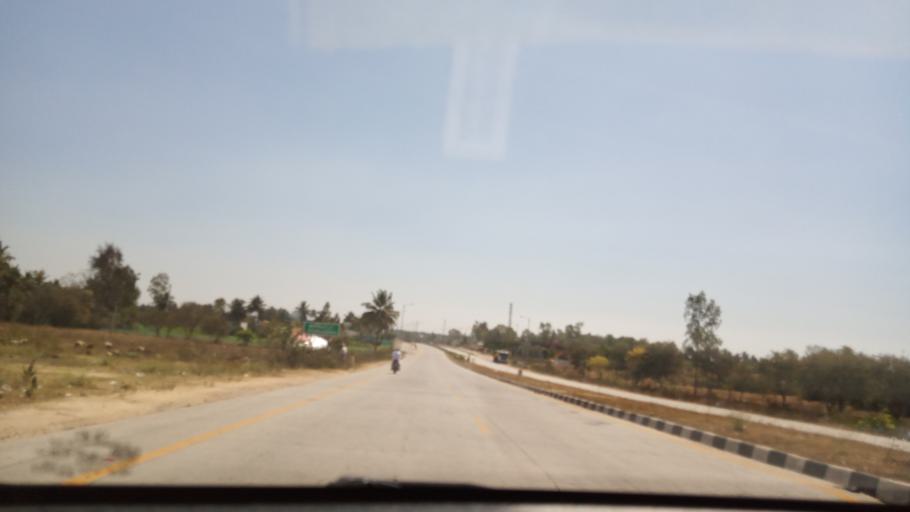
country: IN
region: Karnataka
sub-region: Kolar
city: Mulbagal
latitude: 13.1940
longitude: 78.5560
